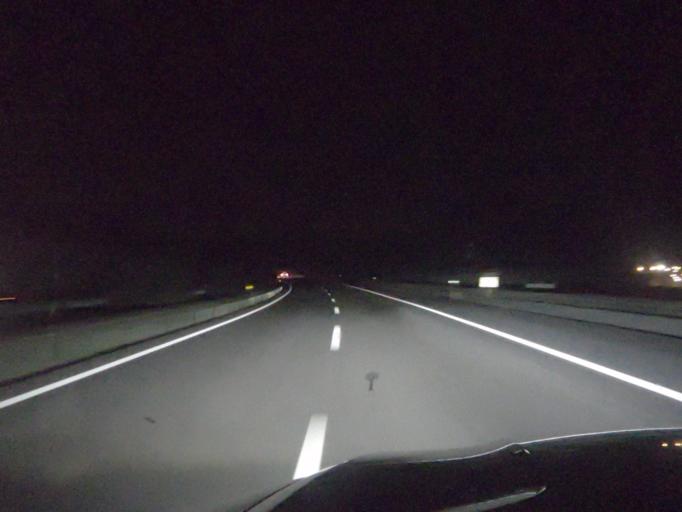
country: PT
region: Aveiro
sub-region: Mealhada
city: Pampilhosa do Botao
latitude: 40.2803
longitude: -8.4777
